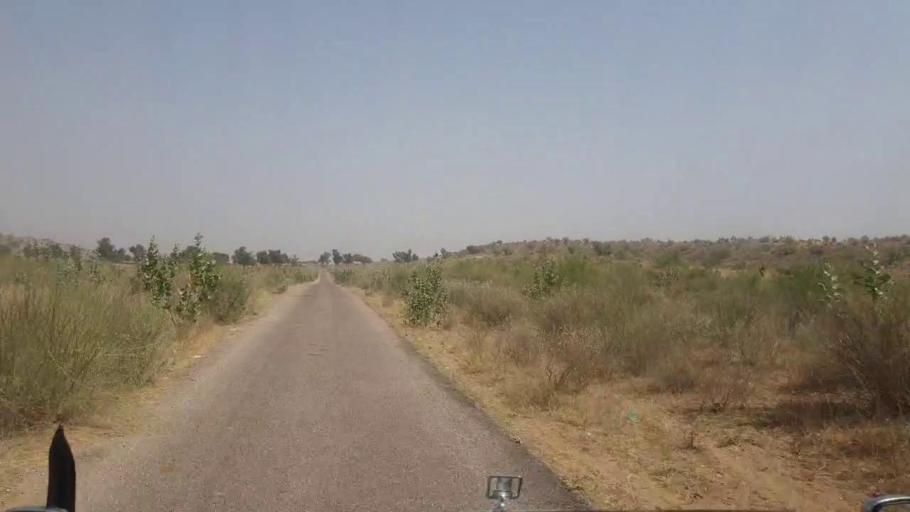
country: PK
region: Sindh
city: Islamkot
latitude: 25.1936
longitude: 70.2053
